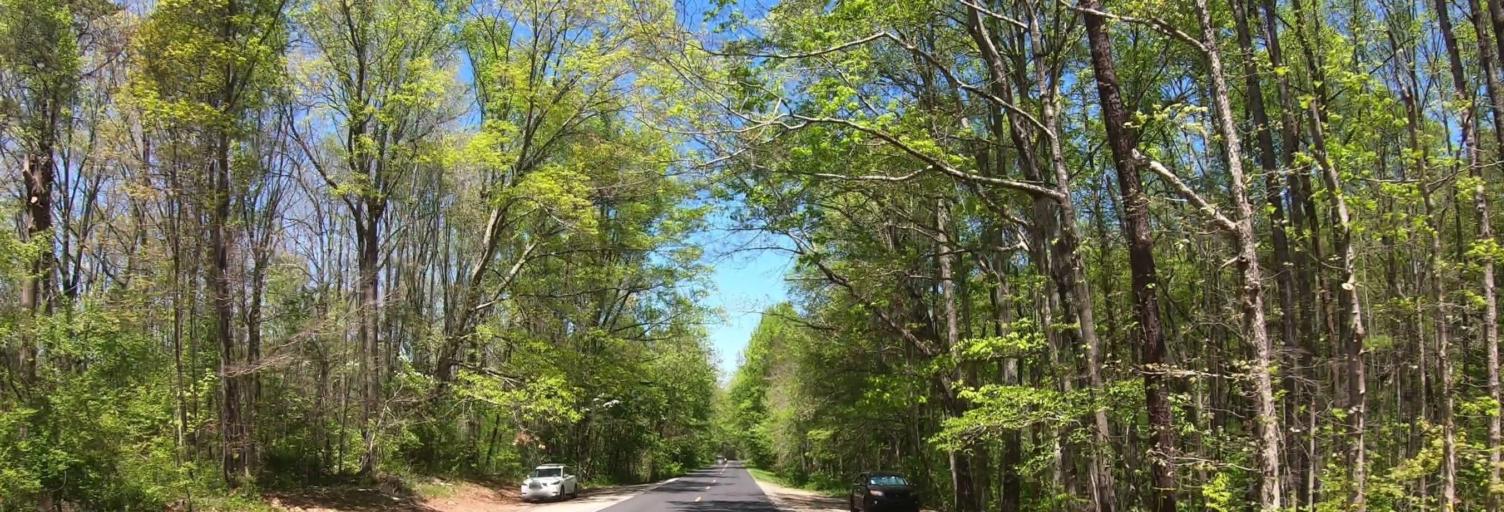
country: US
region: North Carolina
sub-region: Buncombe County
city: Biltmore Forest
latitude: 35.5569
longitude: -82.4959
